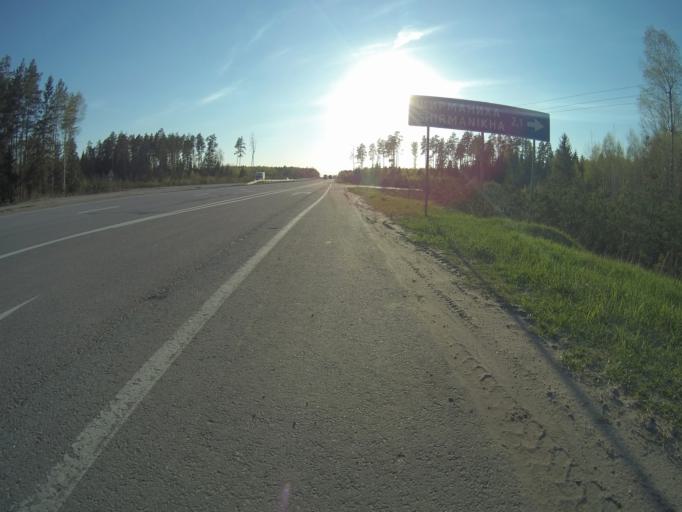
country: RU
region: Vladimir
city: Orgtrud
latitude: 56.1039
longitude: 40.6557
